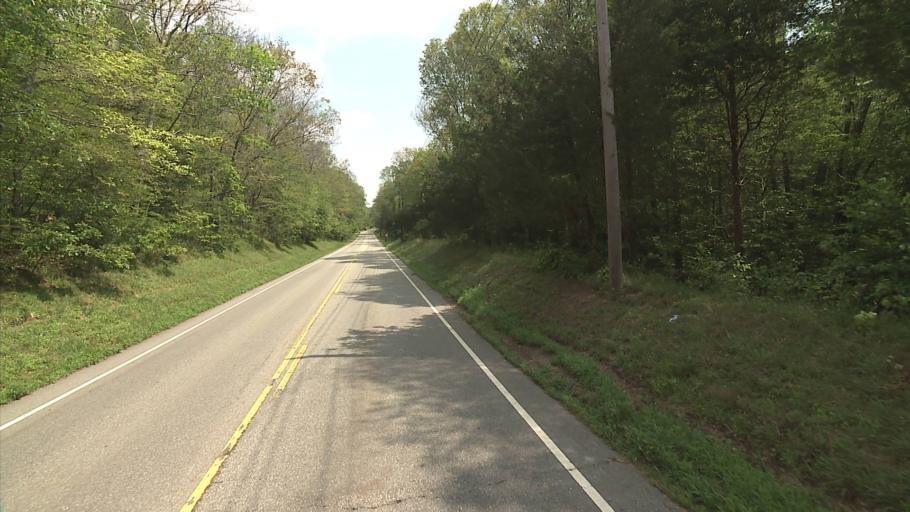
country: US
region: Connecticut
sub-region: New London County
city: Preston City
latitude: 41.5380
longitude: -71.9248
